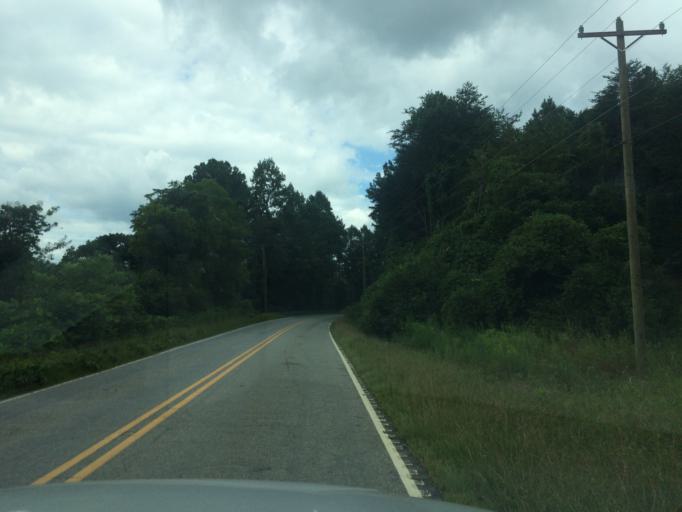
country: US
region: North Carolina
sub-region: Polk County
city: Columbus
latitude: 35.3114
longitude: -82.1688
